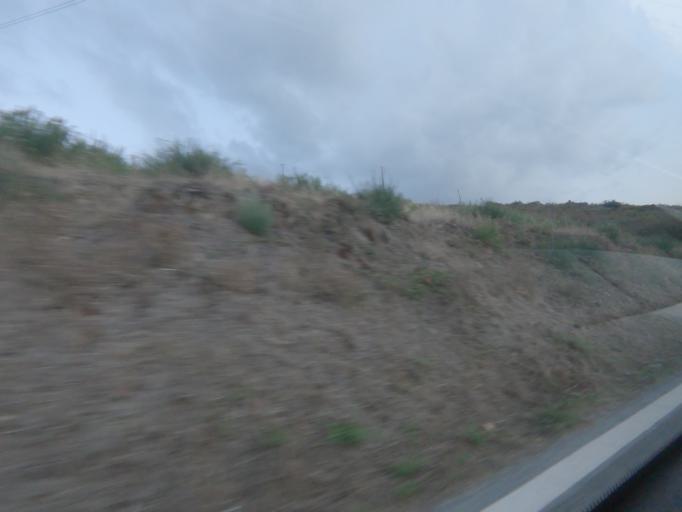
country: PT
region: Vila Real
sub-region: Peso da Regua
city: Peso da Regua
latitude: 41.1364
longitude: -7.7674
